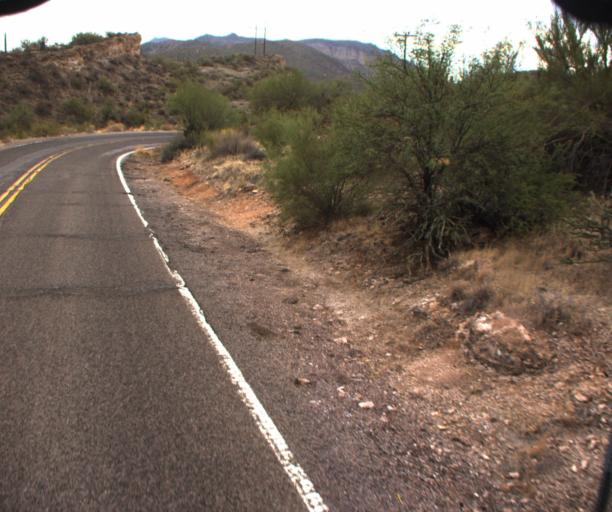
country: US
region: Arizona
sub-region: Pinal County
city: Apache Junction
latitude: 33.5358
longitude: -111.4317
